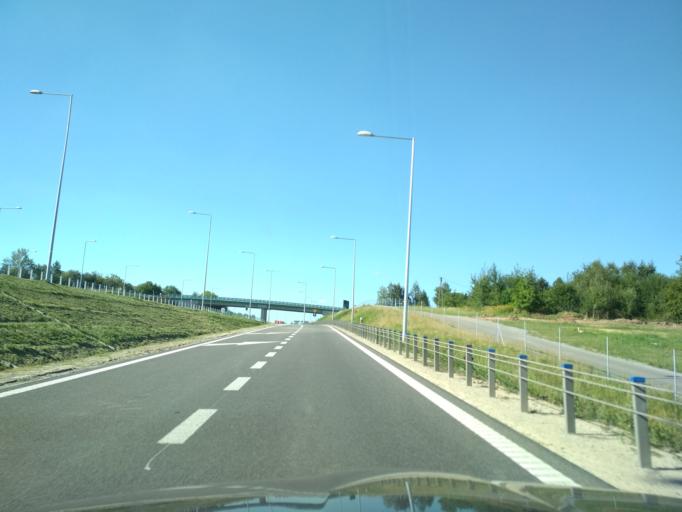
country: PL
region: Subcarpathian Voivodeship
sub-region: Powiat rzeszowski
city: Kielanowka
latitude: 50.0155
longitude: 21.9219
